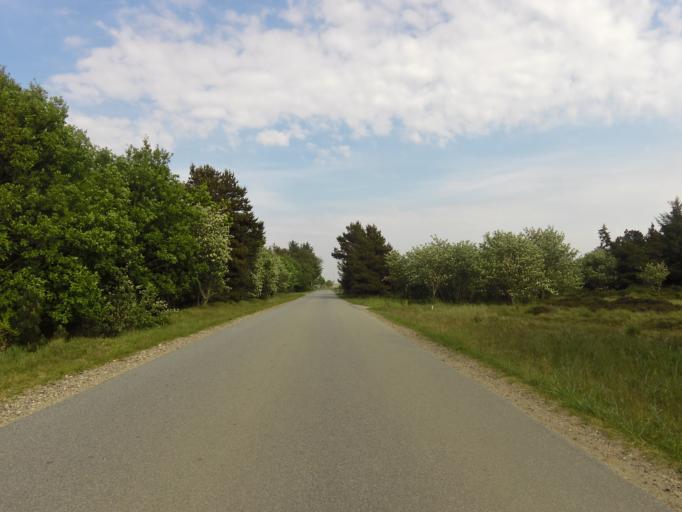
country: DE
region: Schleswig-Holstein
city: List
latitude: 55.1625
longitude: 8.5506
